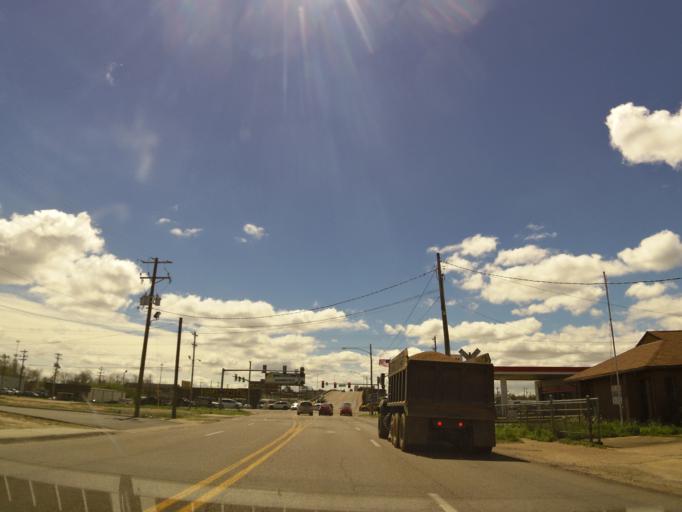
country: US
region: Arkansas
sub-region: Craighead County
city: Jonesboro
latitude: 35.8462
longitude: -90.7047
